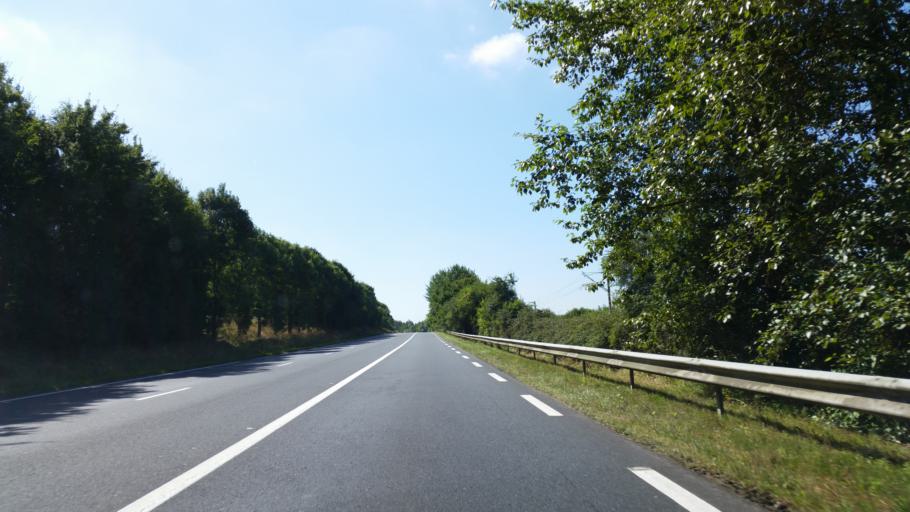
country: FR
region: Lower Normandy
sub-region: Departement du Calvados
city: Saint-Gatien-des-Bois
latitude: 49.2602
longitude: 0.2177
